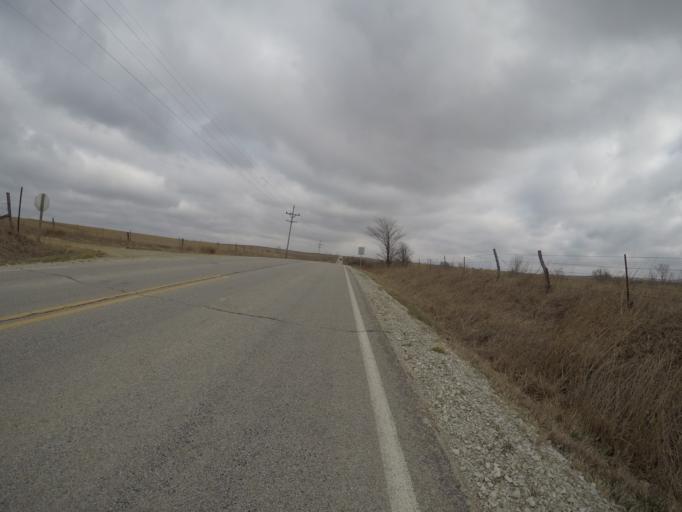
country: US
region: Kansas
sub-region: Pottawatomie County
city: Westmoreland
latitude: 39.3701
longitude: -96.4268
